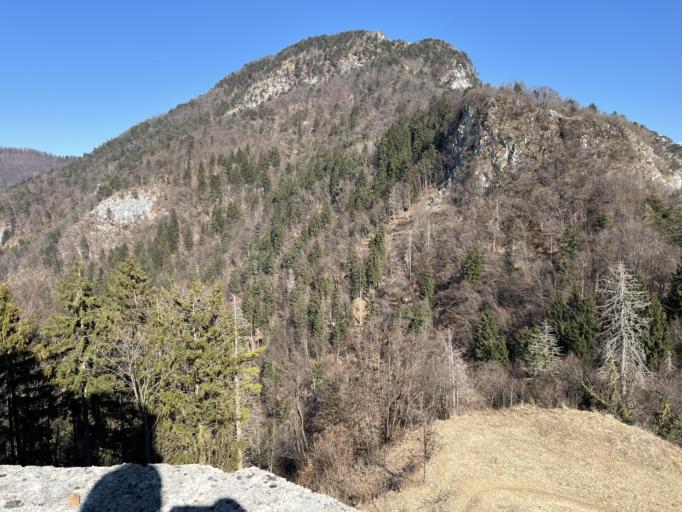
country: IT
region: Friuli Venezia Giulia
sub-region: Provincia di Udine
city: Zuglio
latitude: 46.4367
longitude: 13.0447
